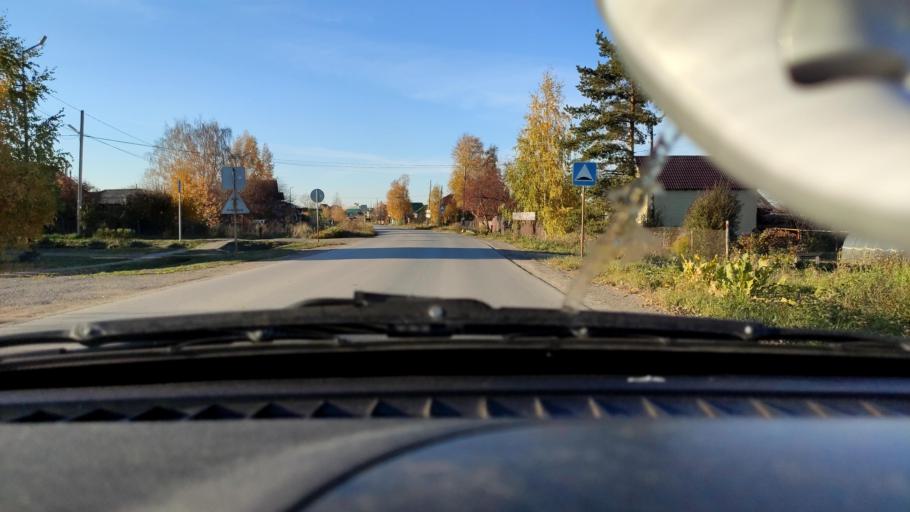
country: RU
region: Perm
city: Froly
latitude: 57.8824
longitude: 56.2613
